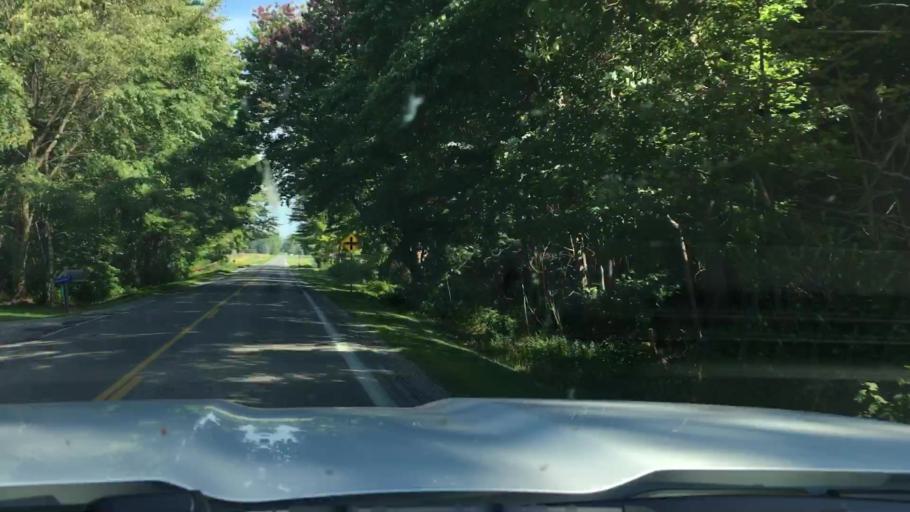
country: US
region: Michigan
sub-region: Saginaw County
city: Hemlock
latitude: 43.4633
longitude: -84.2303
